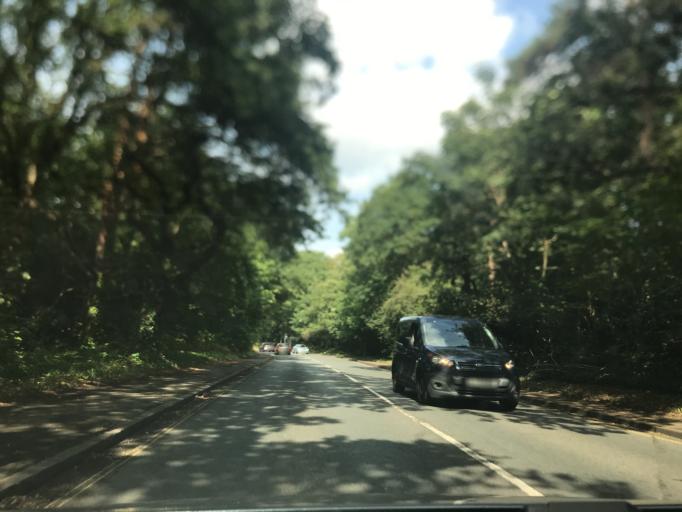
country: GB
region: England
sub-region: Surrey
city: Weybridge
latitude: 51.3600
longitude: -0.4570
